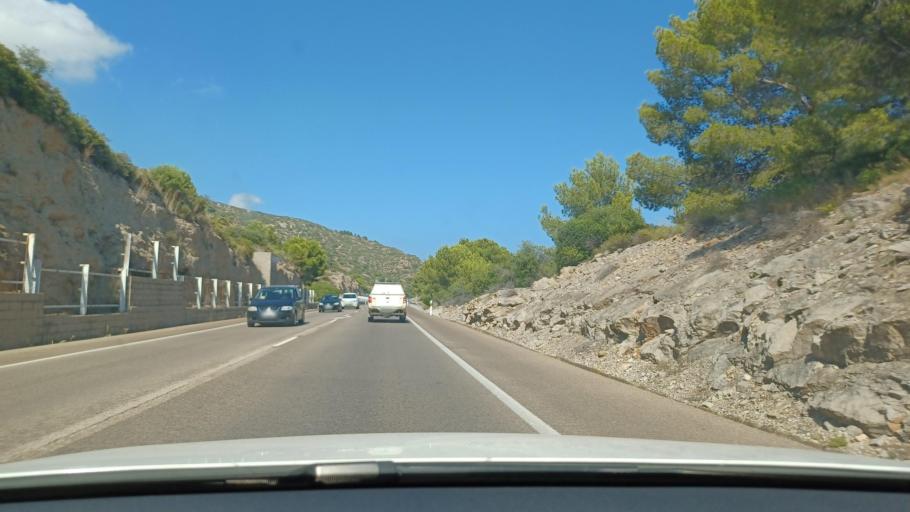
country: ES
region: Valencia
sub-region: Provincia de Castello
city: Benicassim
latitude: 40.0684
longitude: 0.0948
